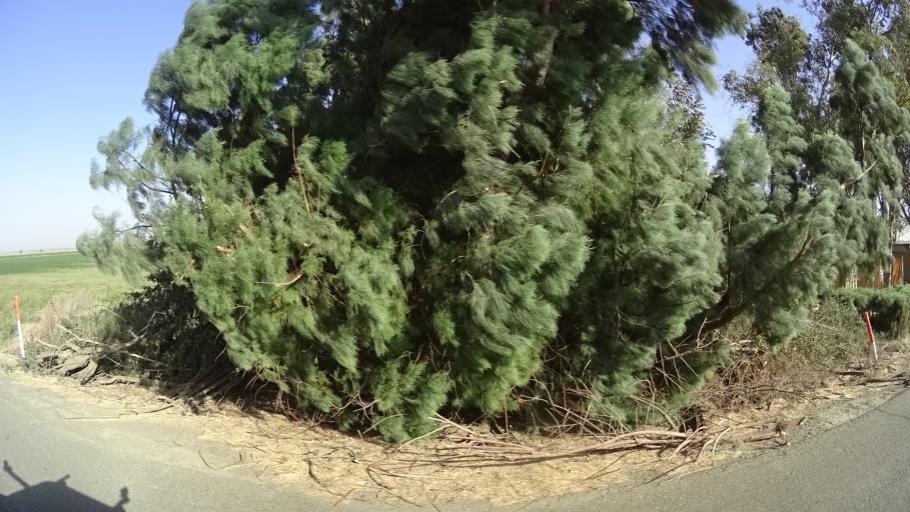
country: US
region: California
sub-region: Yolo County
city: Woodland
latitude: 38.7429
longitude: -121.7294
